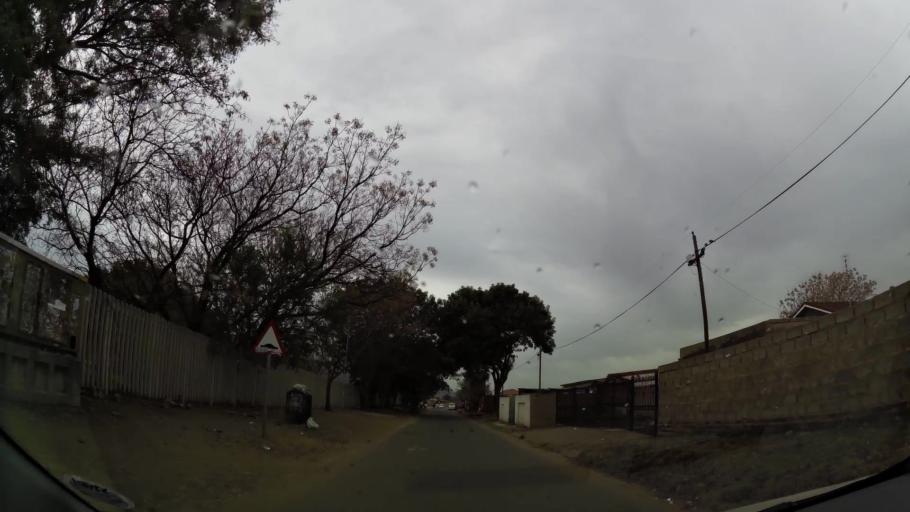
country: ZA
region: Gauteng
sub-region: City of Tshwane Metropolitan Municipality
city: Pretoria
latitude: -25.7080
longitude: 28.3523
